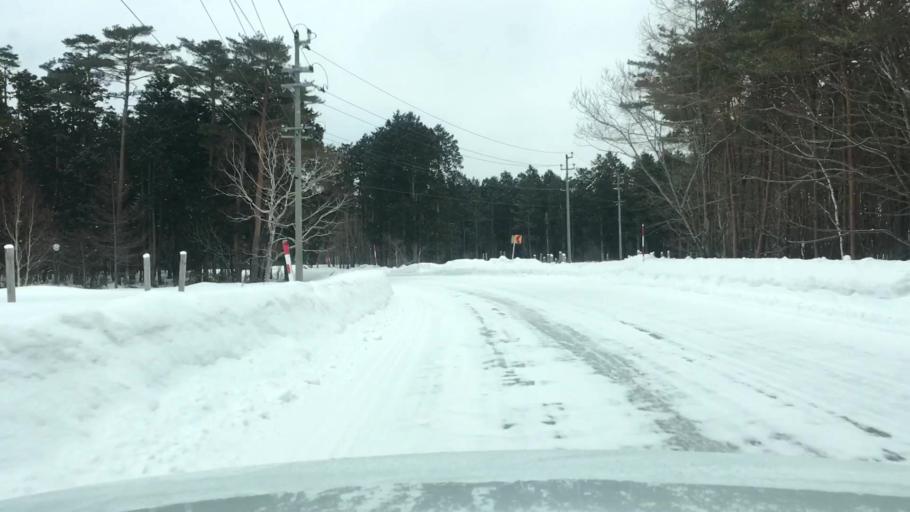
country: JP
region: Iwate
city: Shizukuishi
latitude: 39.9825
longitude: 141.0033
